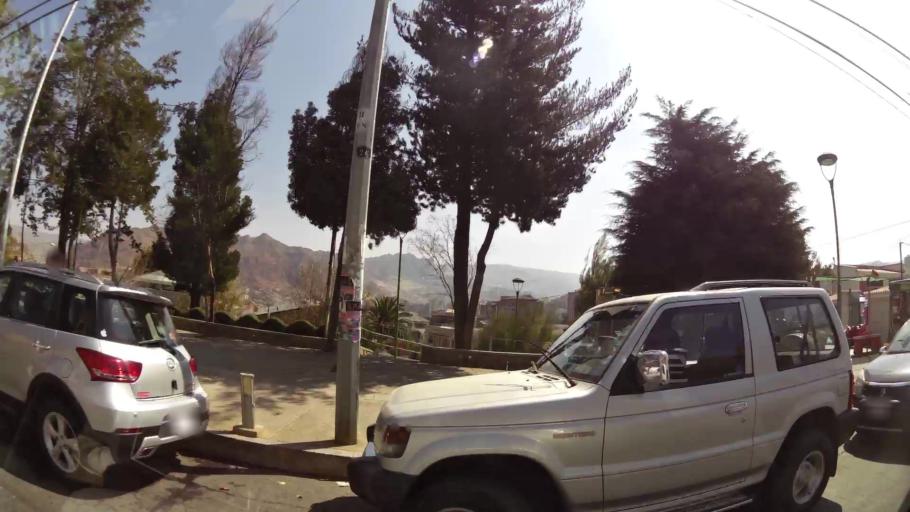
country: BO
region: La Paz
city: La Paz
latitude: -16.5418
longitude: -68.0810
